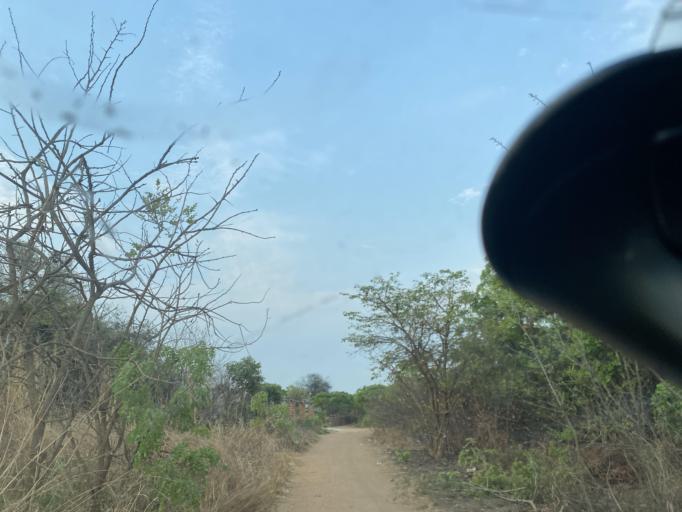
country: ZM
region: Lusaka
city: Chongwe
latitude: -15.2077
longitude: 28.5007
